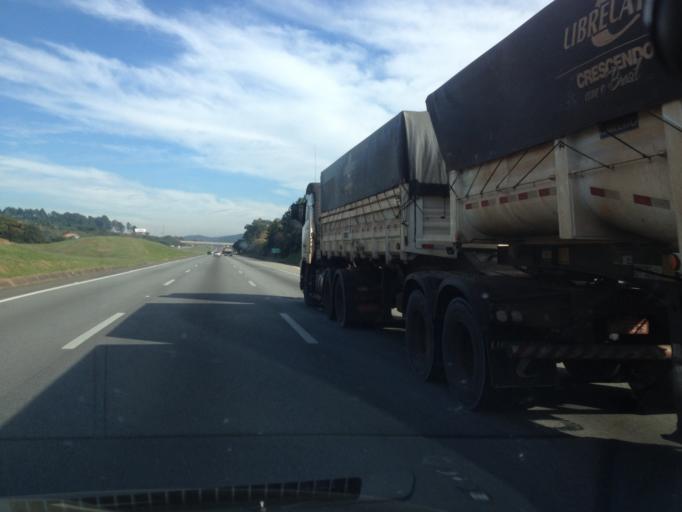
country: BR
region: Sao Paulo
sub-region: Sao Roque
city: Sao Roque
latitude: -23.4196
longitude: -47.1970
